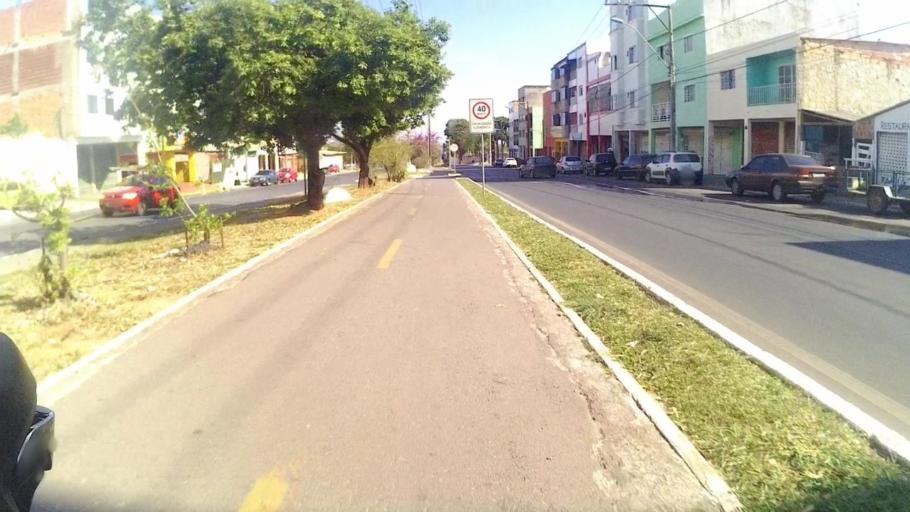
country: BR
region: Federal District
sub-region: Brasilia
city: Brasilia
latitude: -15.7817
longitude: -47.7790
